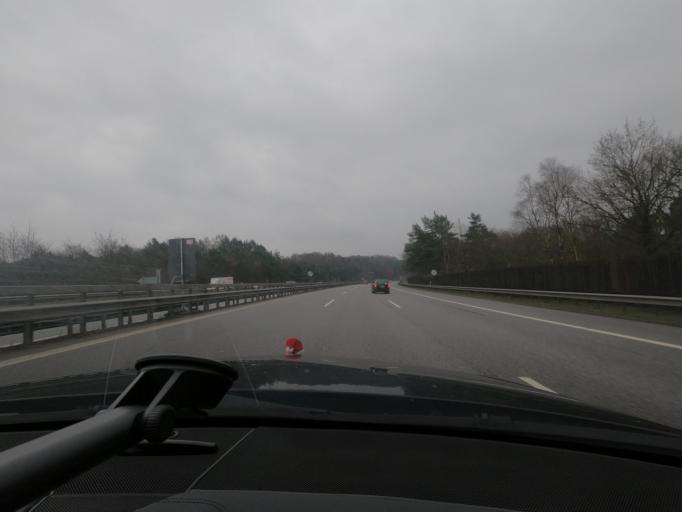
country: DE
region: Hamburg
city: Harburg
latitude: 53.4650
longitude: 9.9268
